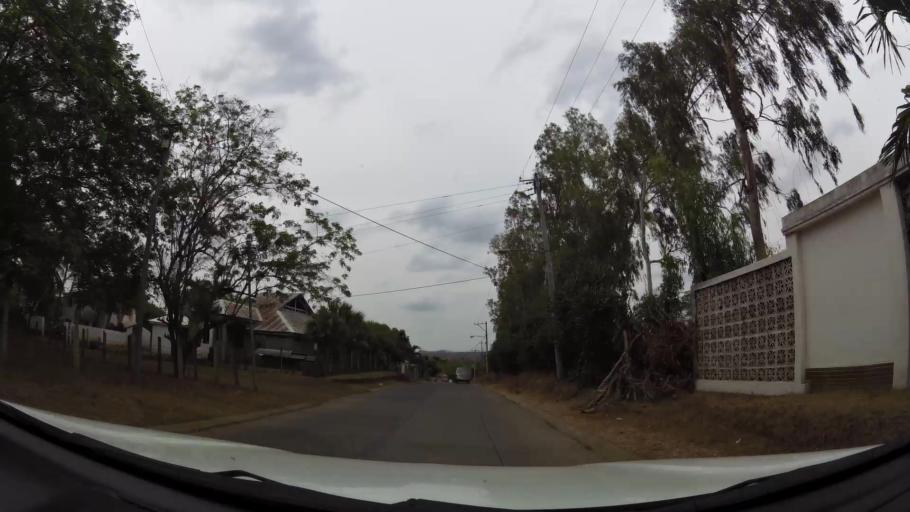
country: NI
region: Masaya
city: Ticuantepe
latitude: 12.0720
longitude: -86.1803
